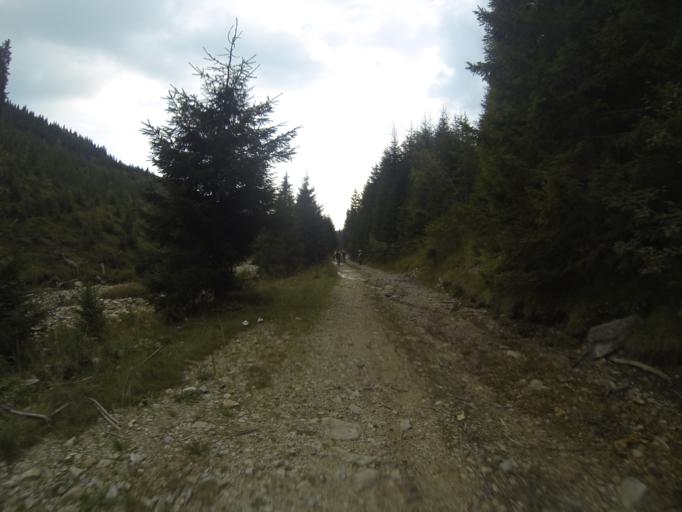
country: RO
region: Gorj
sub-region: Comuna Polovragi
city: Polovragi
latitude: 45.2903
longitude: 23.8440
